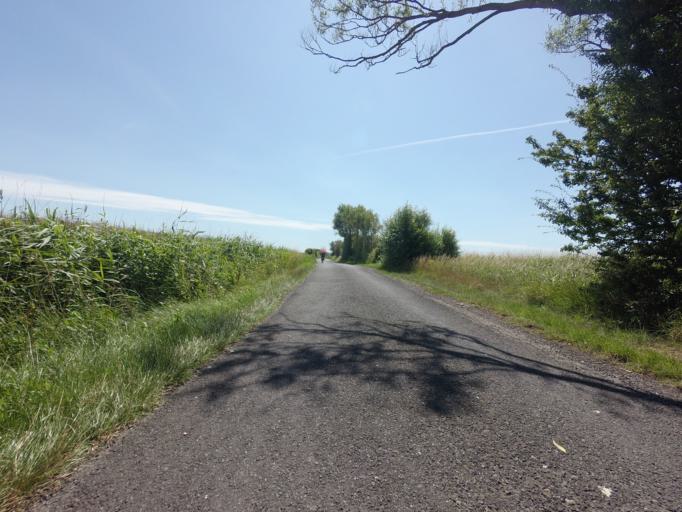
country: GB
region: England
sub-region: Kent
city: Lydd
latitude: 50.9808
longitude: 0.8955
